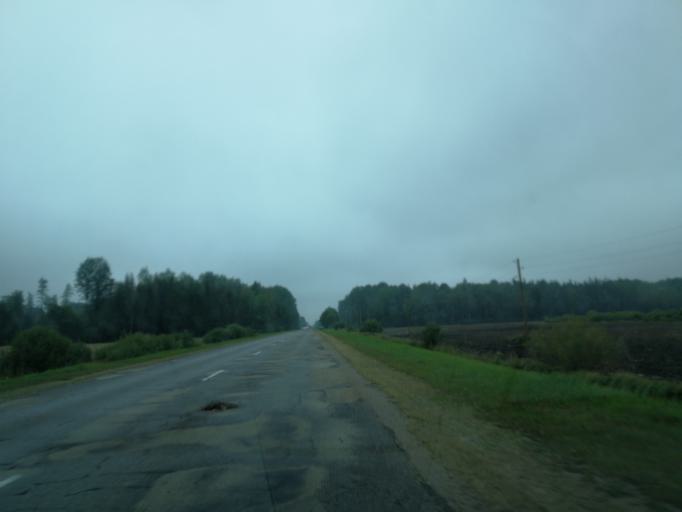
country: LV
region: Varkava
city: Vecvarkava
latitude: 56.3197
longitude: 26.4458
